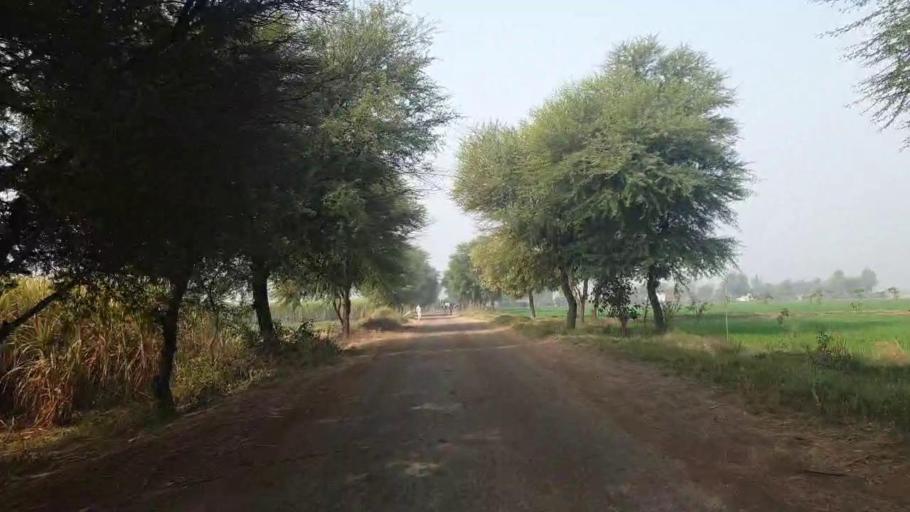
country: PK
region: Sindh
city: Tando Adam
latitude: 25.8042
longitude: 68.6158
